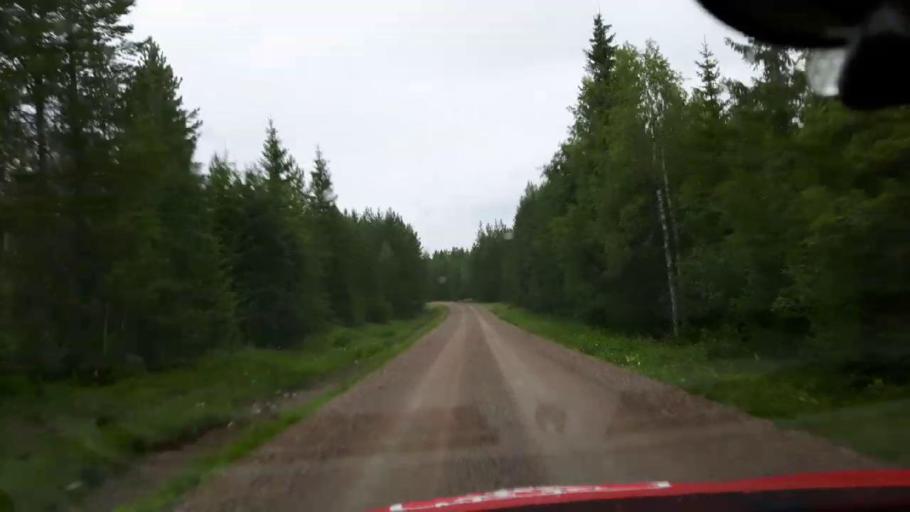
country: SE
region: Jaemtland
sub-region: OEstersunds Kommun
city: Brunflo
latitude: 62.8063
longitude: 14.8969
